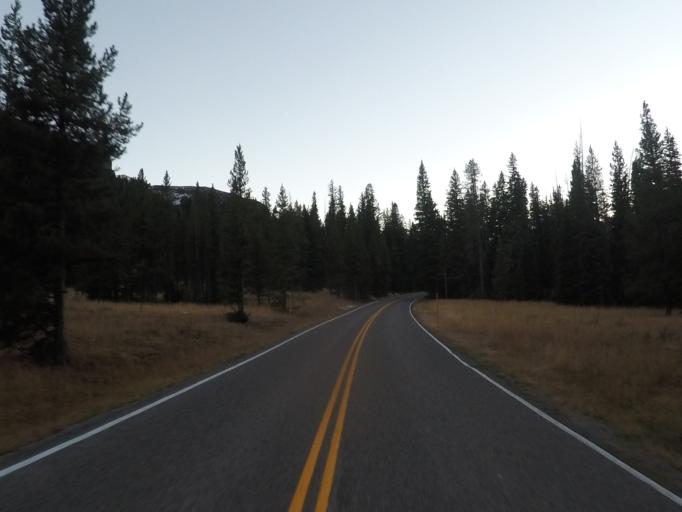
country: US
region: Montana
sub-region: Stillwater County
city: Absarokee
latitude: 44.9873
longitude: -110.0566
